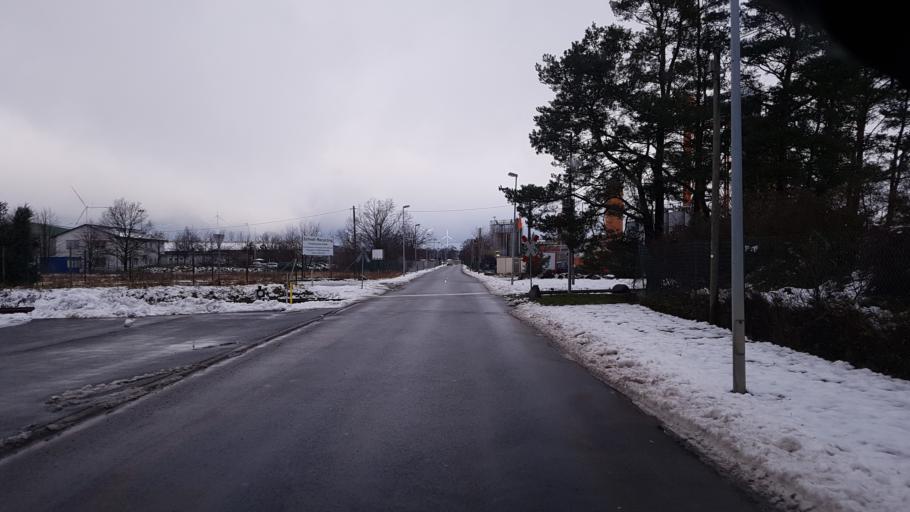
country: DE
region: Brandenburg
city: Luckau
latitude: 51.8769
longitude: 13.7980
